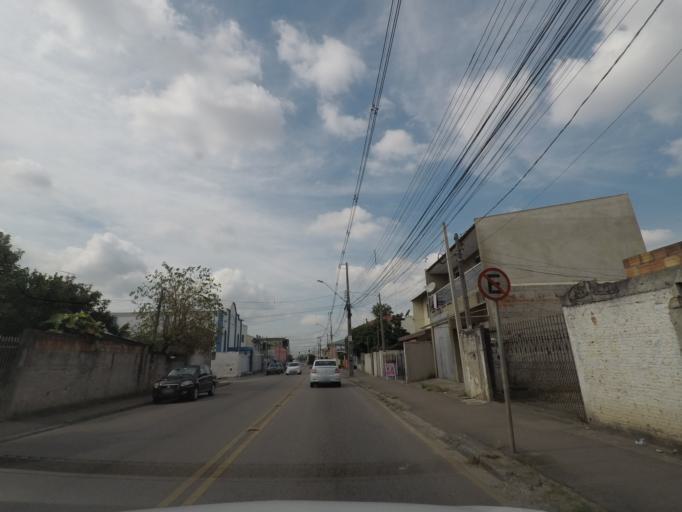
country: BR
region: Parana
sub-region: Pinhais
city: Pinhais
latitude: -25.4668
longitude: -49.1966
